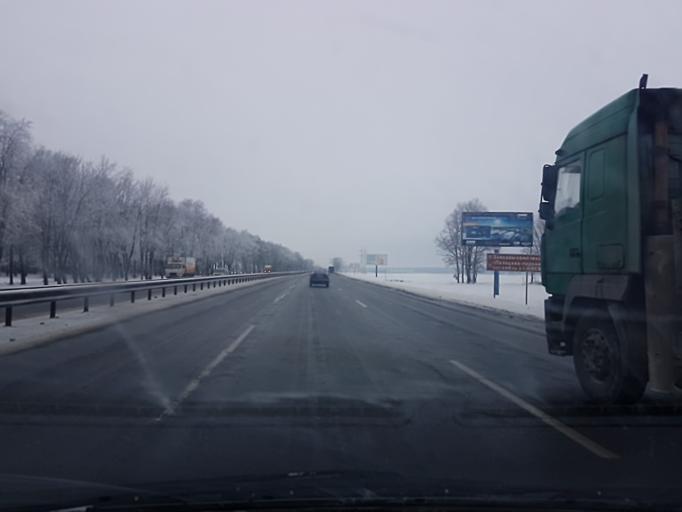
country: BY
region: Minsk
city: Shchomyslitsa
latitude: 53.8316
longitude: 27.4572
